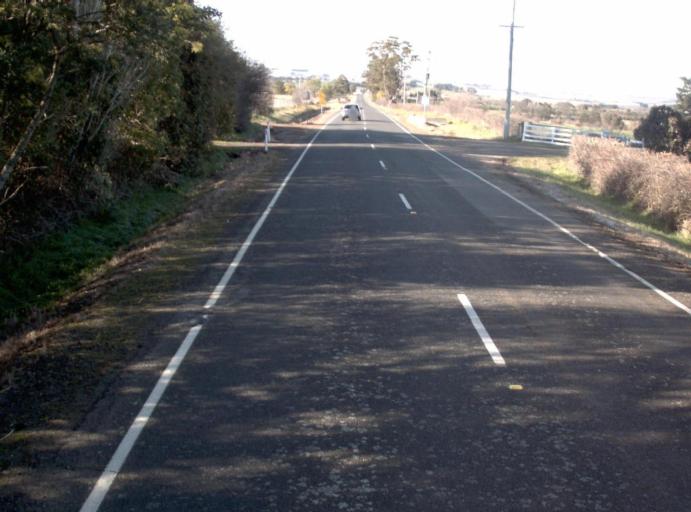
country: AU
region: Tasmania
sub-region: Launceston
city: Newstead
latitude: -41.4703
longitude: 147.2110
